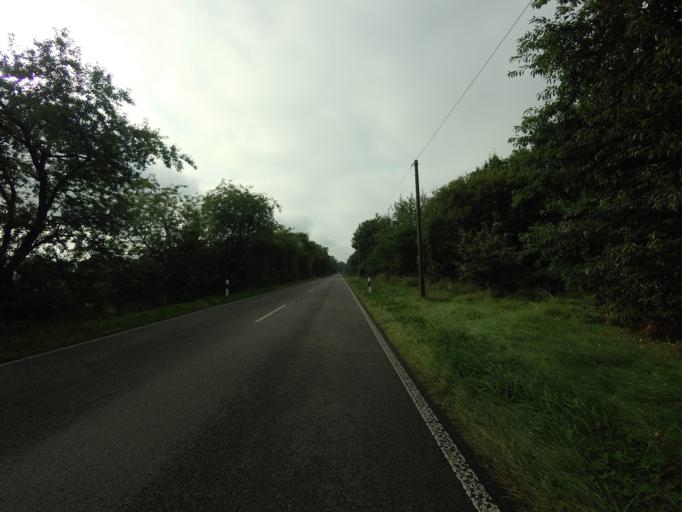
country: DE
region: Lower Saxony
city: Wielen
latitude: 52.4975
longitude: 6.7373
